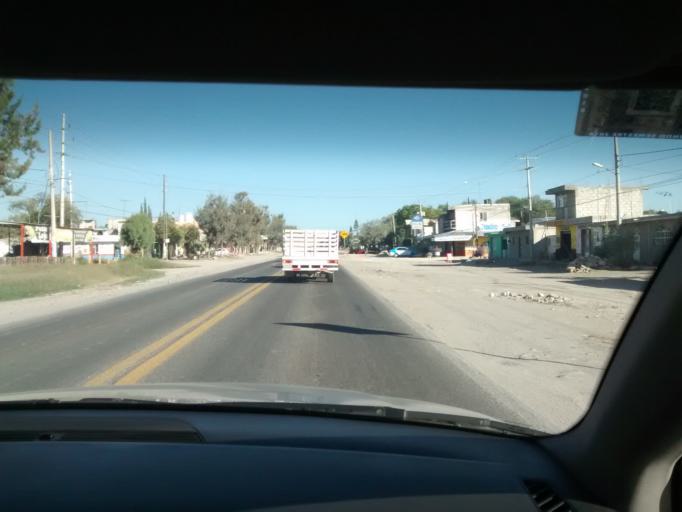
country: MX
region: Puebla
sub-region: Tehuacan
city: Magdalena Cuayucatepec
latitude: 18.5086
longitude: -97.4887
